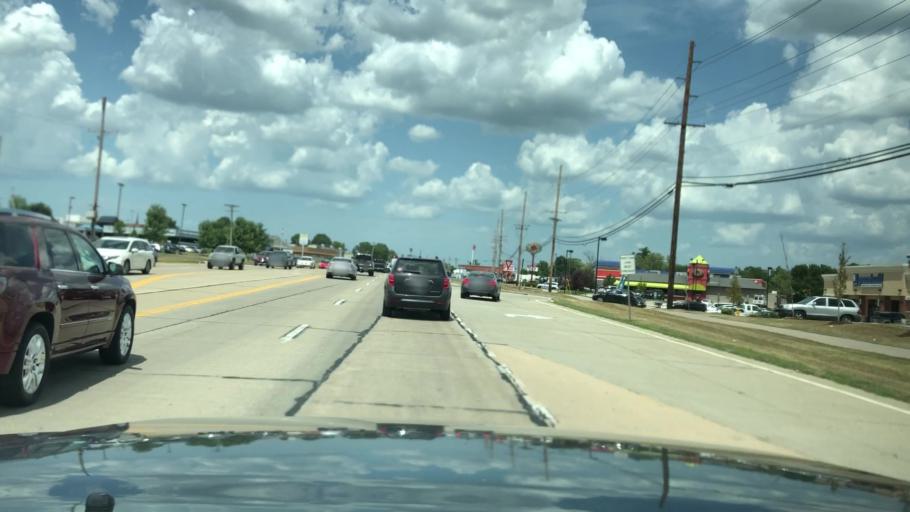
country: US
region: Missouri
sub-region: Saint Charles County
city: O'Fallon
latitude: 38.7945
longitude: -90.6990
